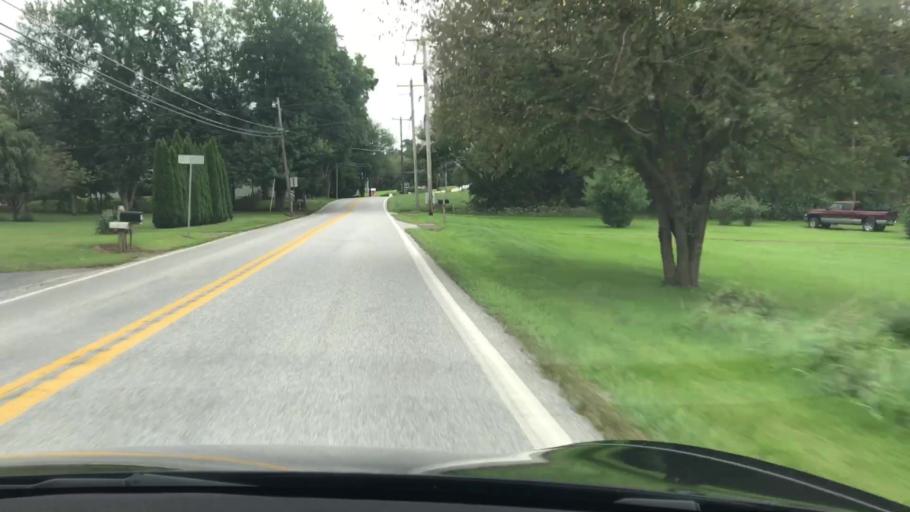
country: US
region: Pennsylvania
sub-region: York County
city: Dillsburg
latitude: 40.1437
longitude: -76.9652
